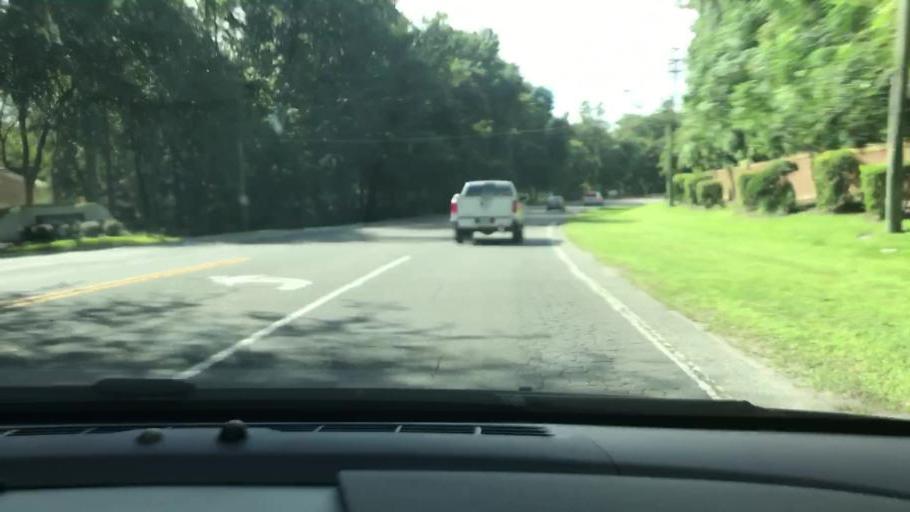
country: US
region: Florida
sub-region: Alachua County
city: Gainesville
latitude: 29.6438
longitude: -82.3991
